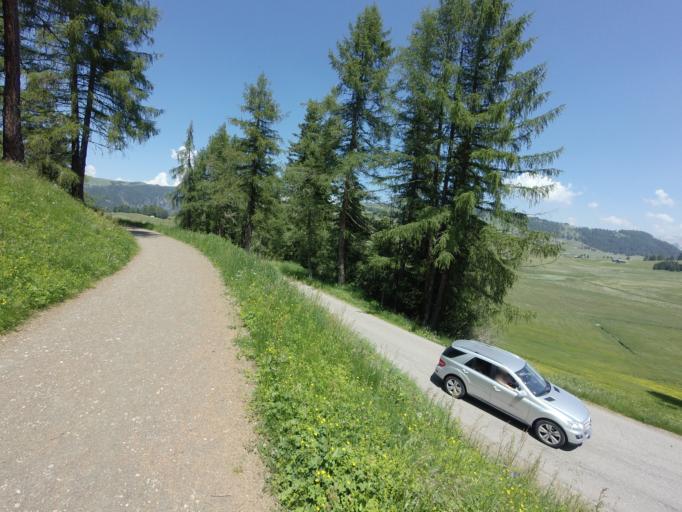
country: IT
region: Trentino-Alto Adige
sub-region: Bolzano
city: Ortisei
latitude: 46.5383
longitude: 11.6508
